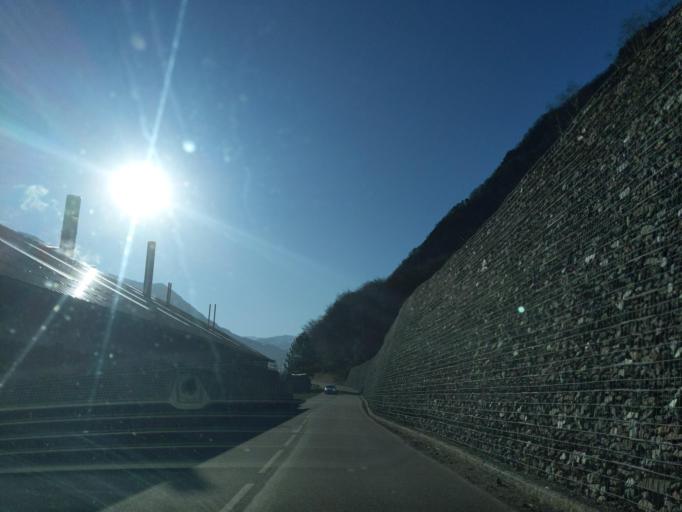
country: FR
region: Rhone-Alpes
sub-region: Departement de la Savoie
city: Aigueblanche
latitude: 45.5275
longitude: 6.4752
